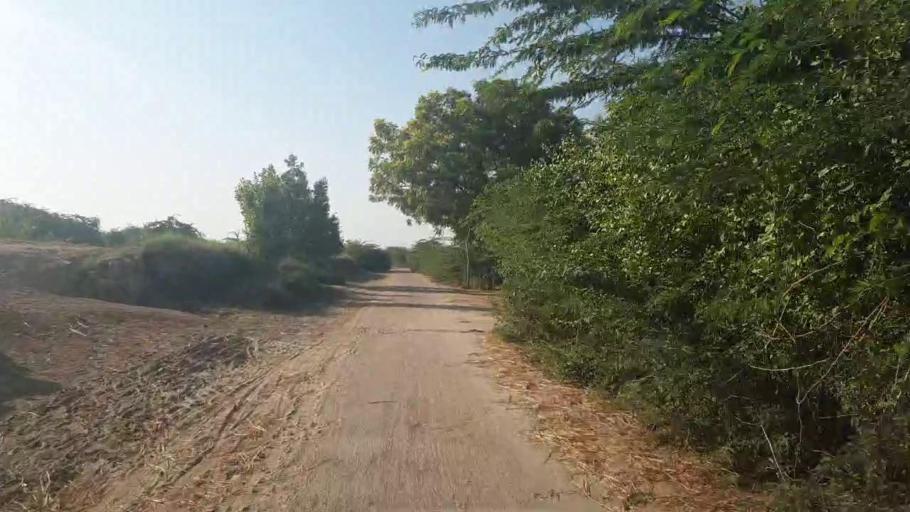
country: PK
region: Sindh
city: Tando Bago
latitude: 24.7423
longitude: 68.9307
